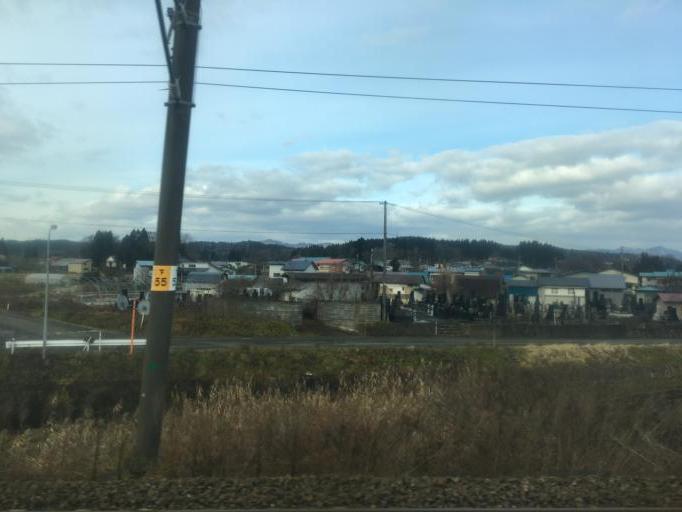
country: JP
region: Akita
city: Takanosu
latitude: 40.2539
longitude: 140.4012
